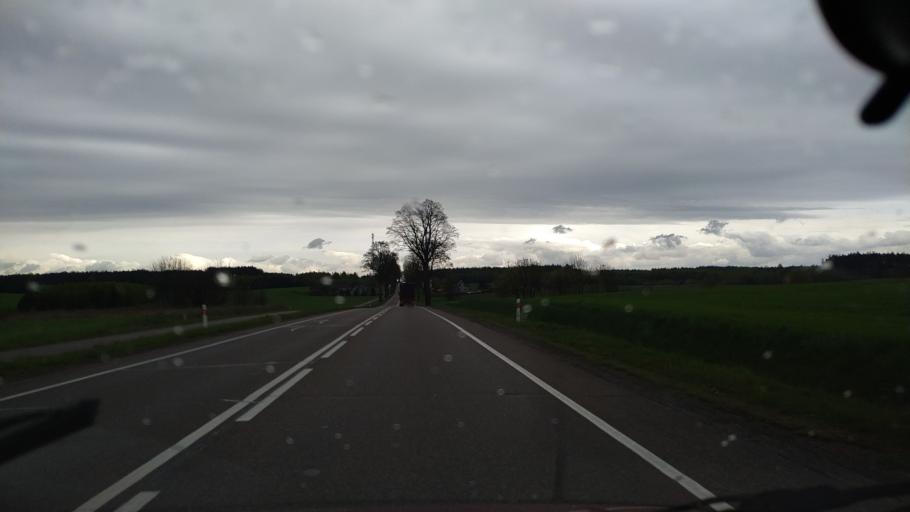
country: PL
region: Pomeranian Voivodeship
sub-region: Powiat starogardzki
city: Kaliska
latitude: 53.8899
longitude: 18.2204
